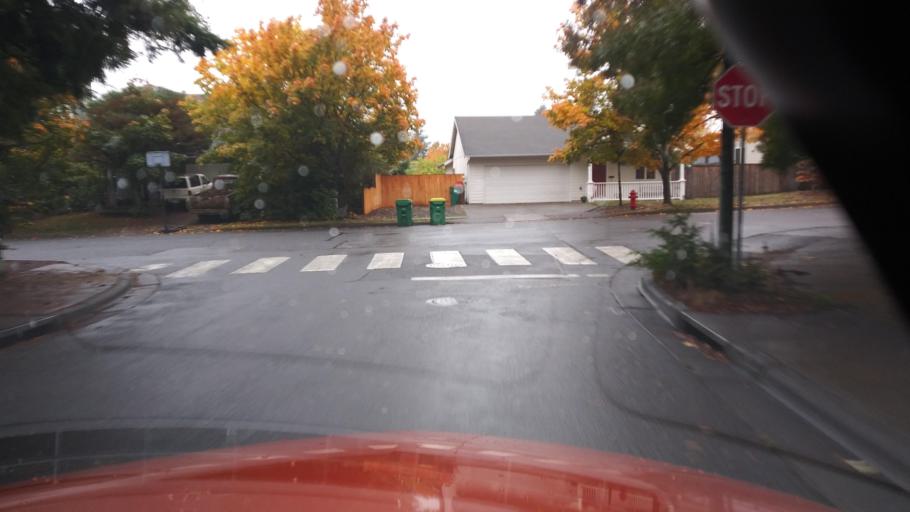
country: US
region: Oregon
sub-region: Washington County
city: Forest Grove
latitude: 45.5340
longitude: -123.1271
